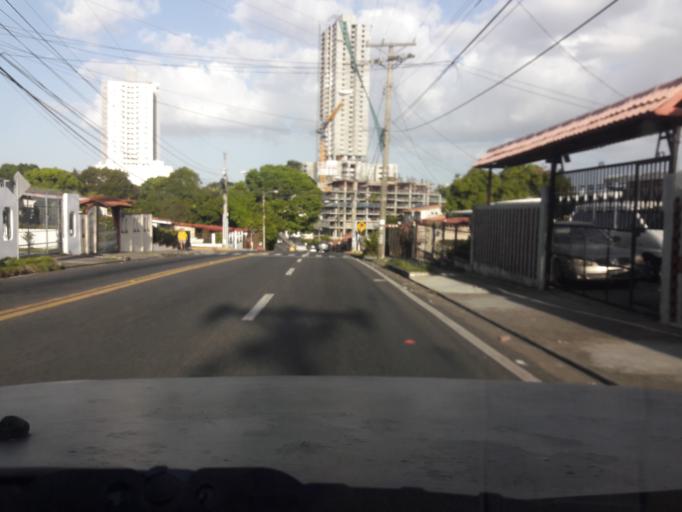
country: PA
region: Panama
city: Panama
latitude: 9.0131
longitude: -79.5099
